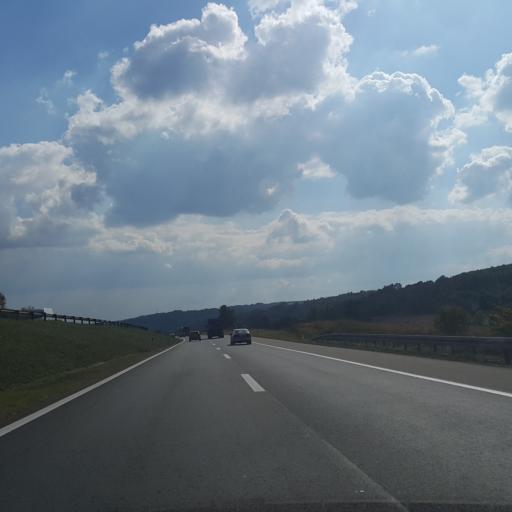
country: RS
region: Central Serbia
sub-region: Belgrade
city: Grocka
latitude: 44.6079
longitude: 20.6406
